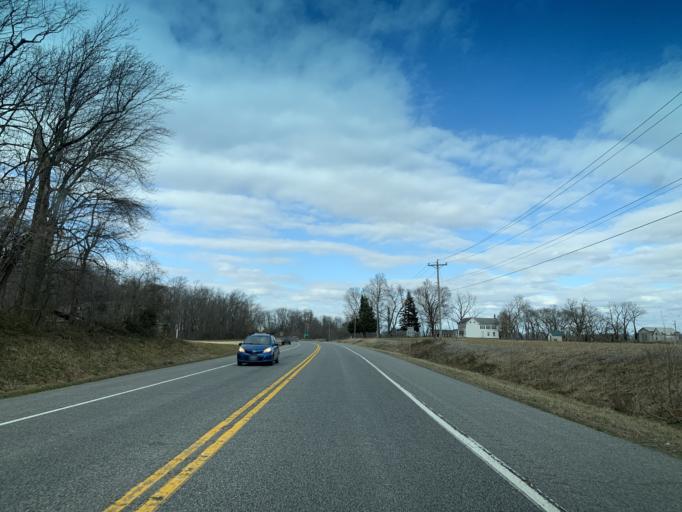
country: US
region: Maryland
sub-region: Queen Anne's County
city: Centreville
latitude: 38.9970
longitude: -76.0743
